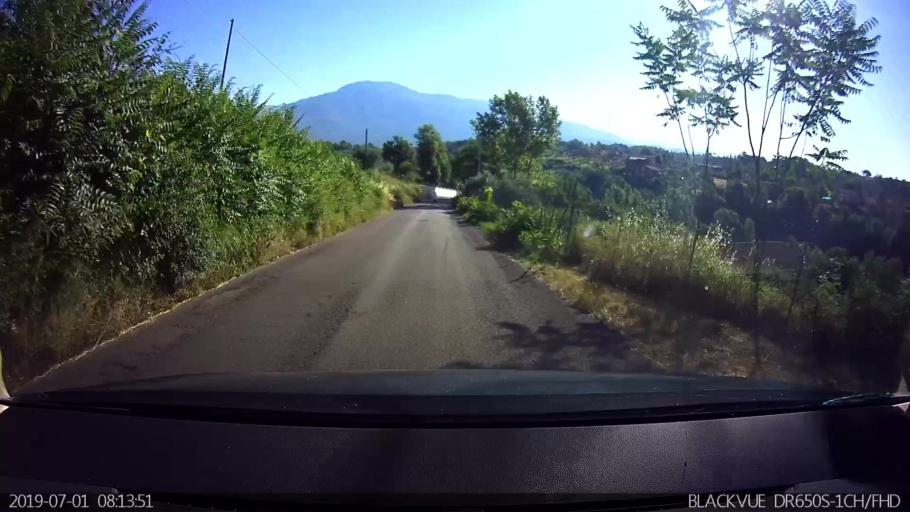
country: IT
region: Latium
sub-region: Provincia di Frosinone
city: Veroli
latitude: 41.6925
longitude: 13.4250
